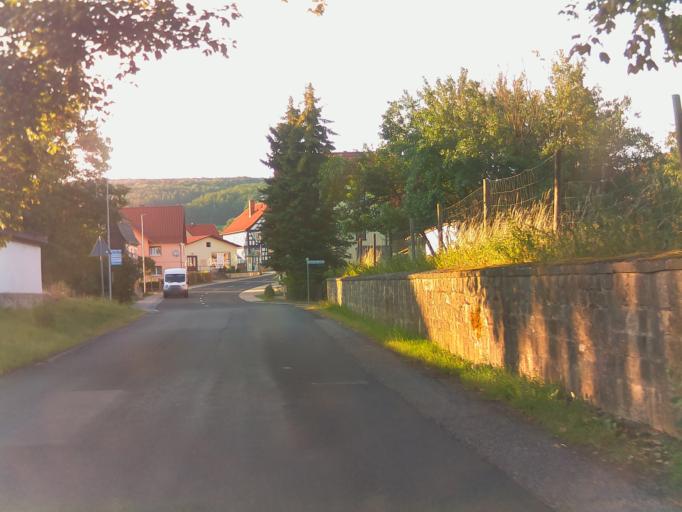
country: DE
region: Thuringia
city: Wolfershausen
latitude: 50.4515
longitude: 10.4017
